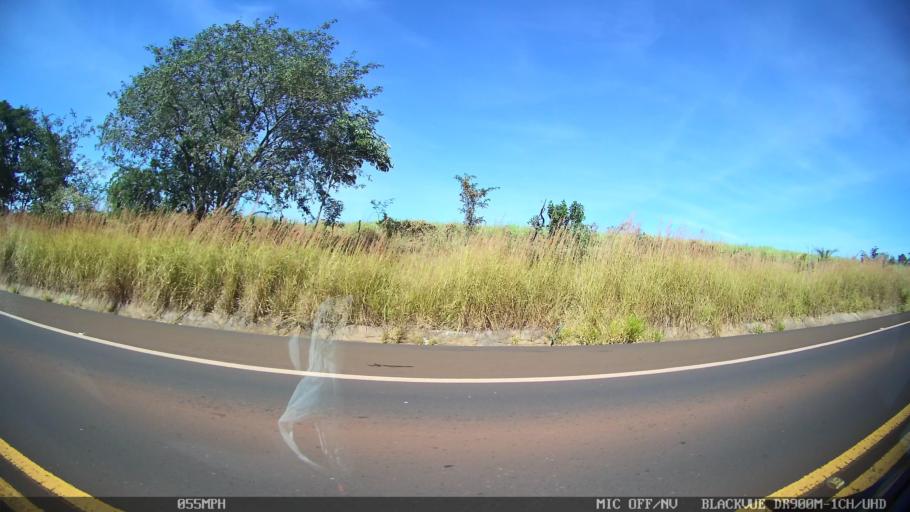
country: BR
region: Sao Paulo
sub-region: Franca
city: Franca
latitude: -20.5609
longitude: -47.5065
